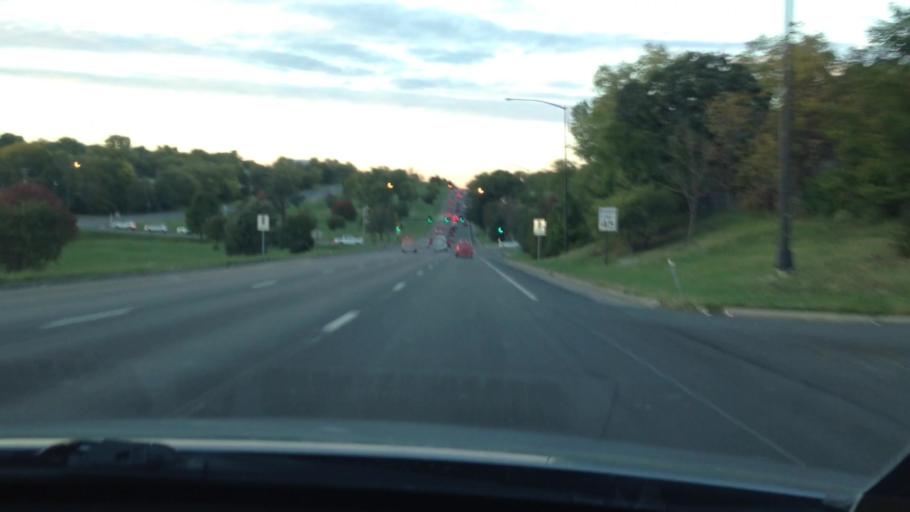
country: US
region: Kansas
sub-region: Johnson County
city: Mission Hills
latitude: 39.0175
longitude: -94.5539
